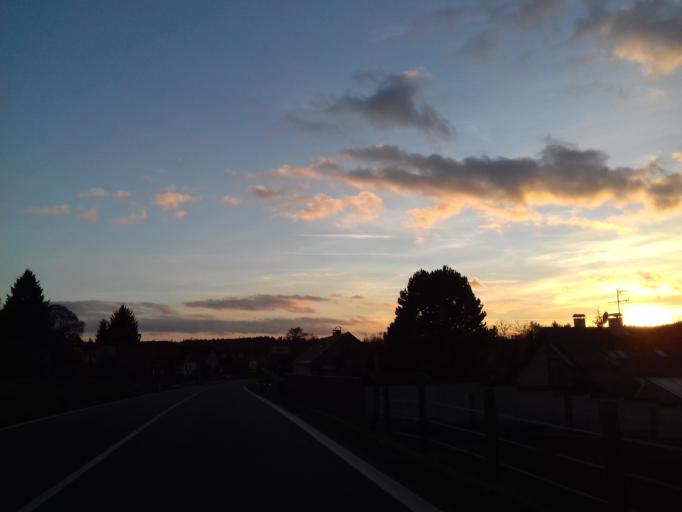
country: CZ
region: Vysocina
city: Krizova
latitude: 49.7192
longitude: 15.8618
